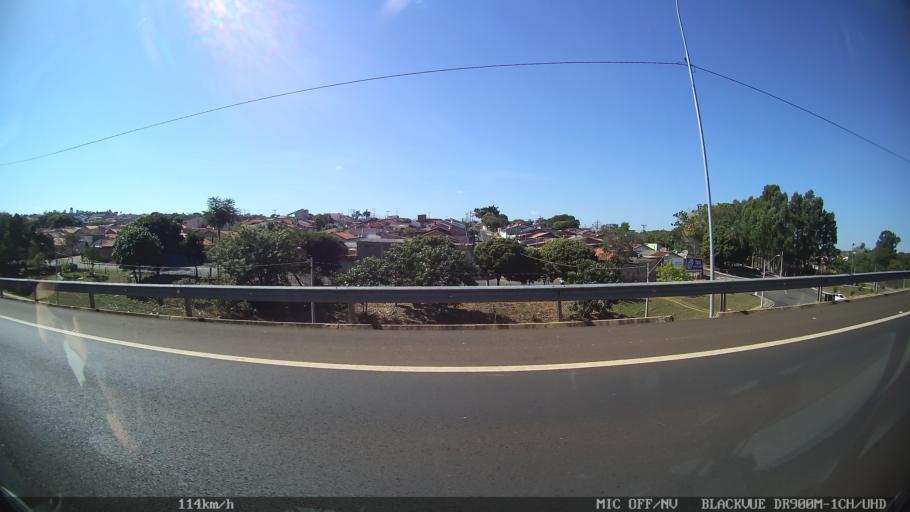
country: BR
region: Sao Paulo
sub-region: Franca
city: Franca
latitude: -20.4893
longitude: -47.4083
